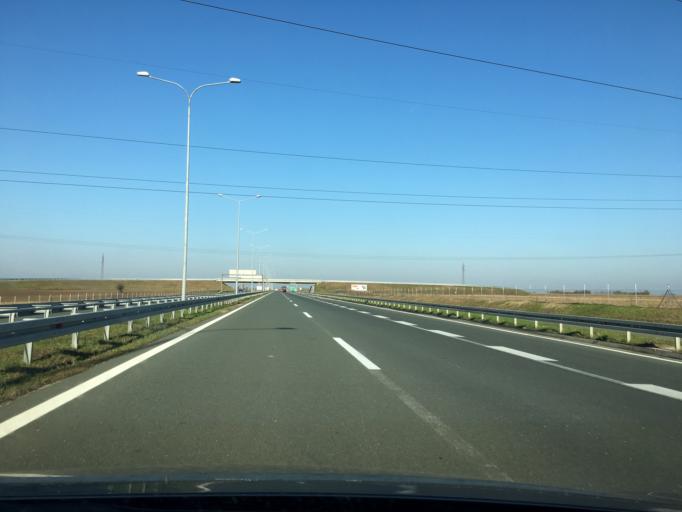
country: RS
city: Rumenka
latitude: 45.3152
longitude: 19.7971
